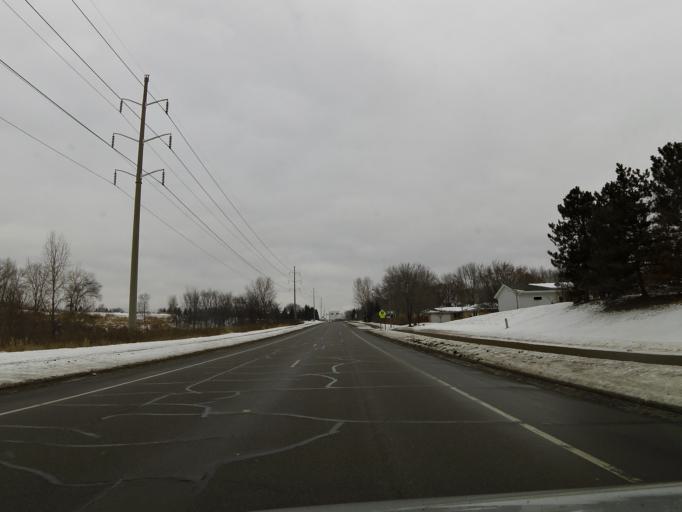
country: US
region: Minnesota
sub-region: Dakota County
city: Burnsville
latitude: 44.7467
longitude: -93.2583
